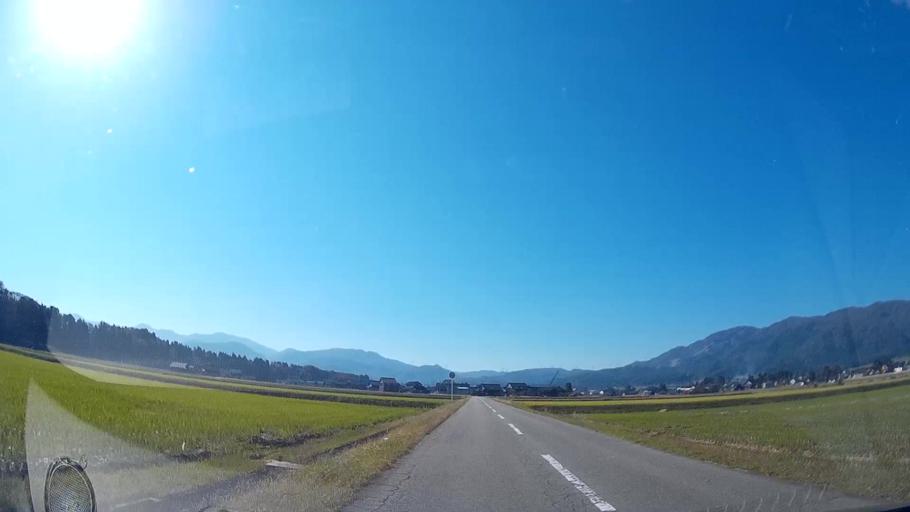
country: JP
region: Toyama
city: Fukumitsu
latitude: 36.5404
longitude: 136.8664
